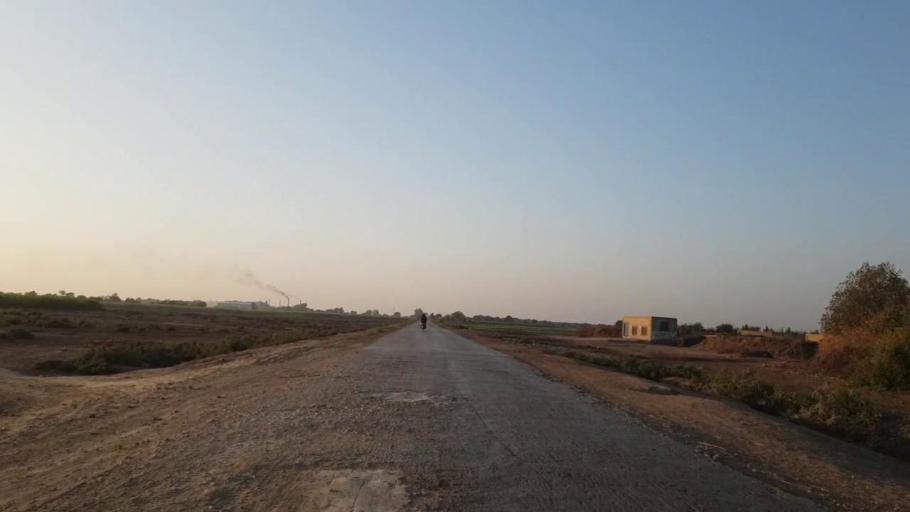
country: PK
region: Sindh
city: Chambar
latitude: 25.2432
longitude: 68.6877
